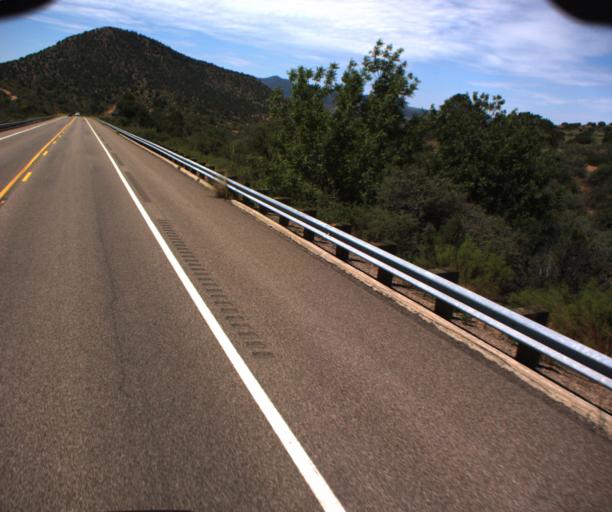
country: US
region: Arizona
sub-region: Gila County
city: Globe
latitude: 33.6166
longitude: -110.6042
